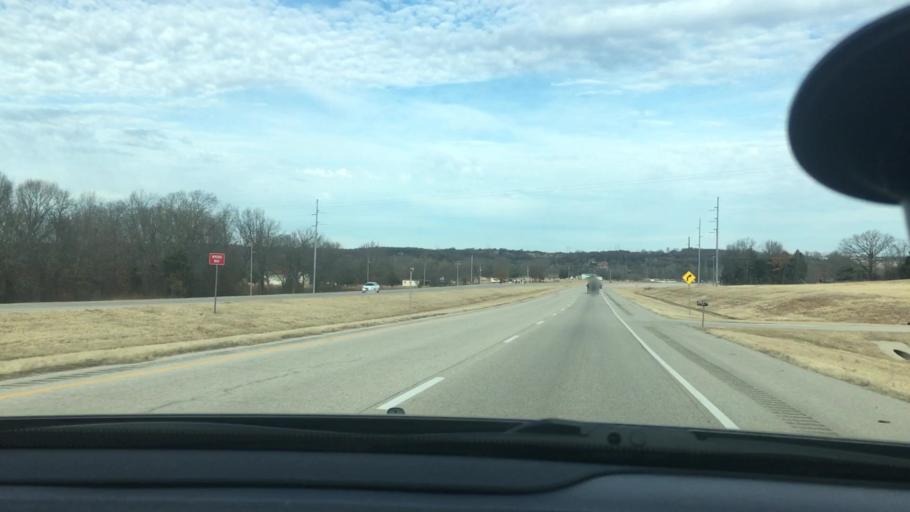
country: US
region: Oklahoma
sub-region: Pontotoc County
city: Byng
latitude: 34.9202
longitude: -96.6824
